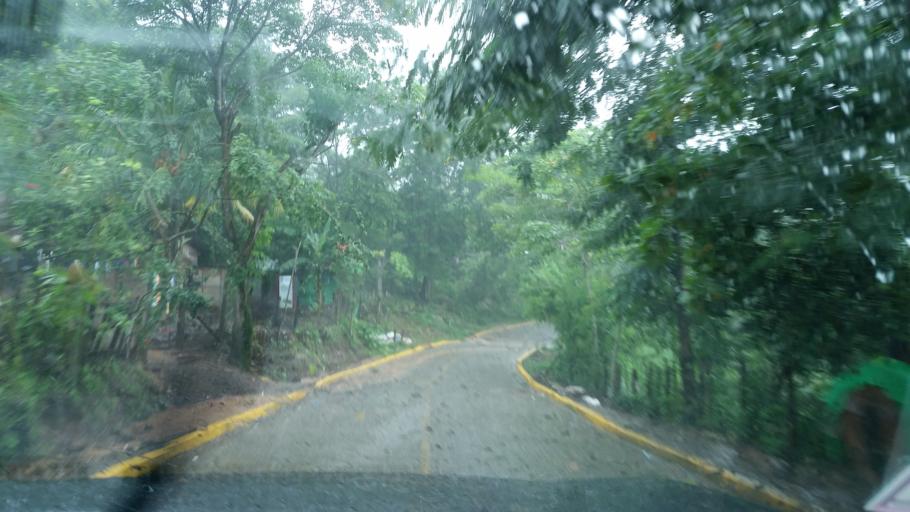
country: NI
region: Atlantico Norte (RAAN)
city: Waslala
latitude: 13.1571
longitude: -85.4408
